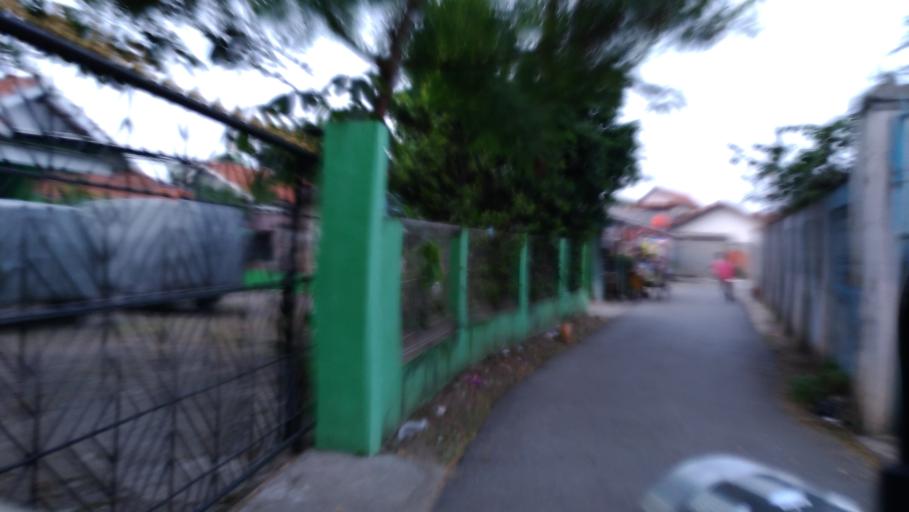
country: ID
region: West Java
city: Depok
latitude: -6.3613
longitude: 106.8673
